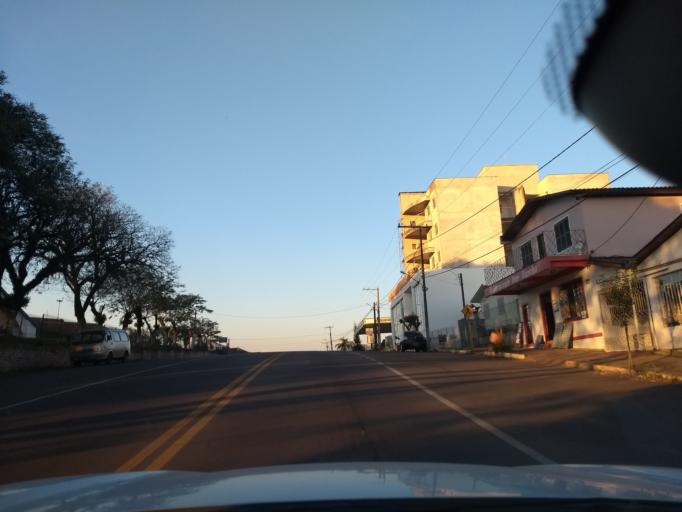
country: BR
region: Rio Grande do Sul
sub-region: Santa Cruz Do Sul
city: Santa Cruz do Sul
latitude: -29.7186
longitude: -52.5114
